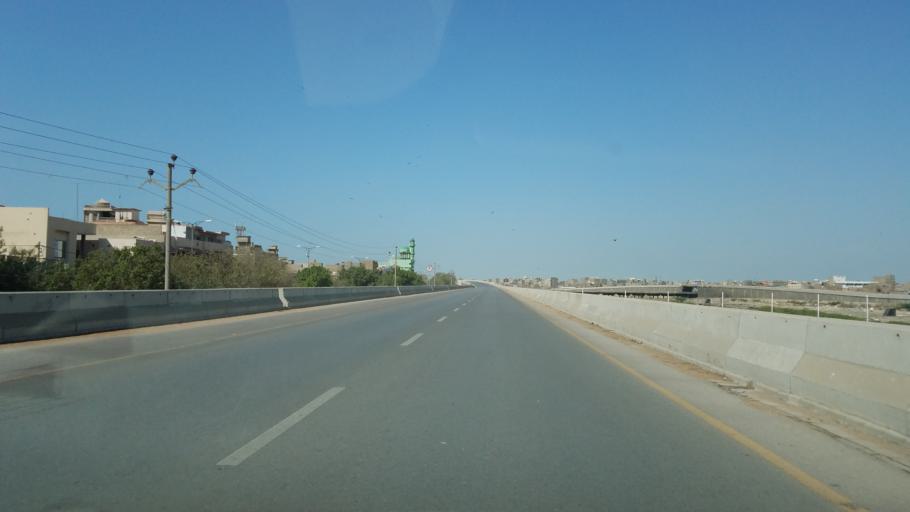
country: PK
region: Sindh
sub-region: Karachi District
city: Karachi
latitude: 24.8804
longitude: 67.0008
